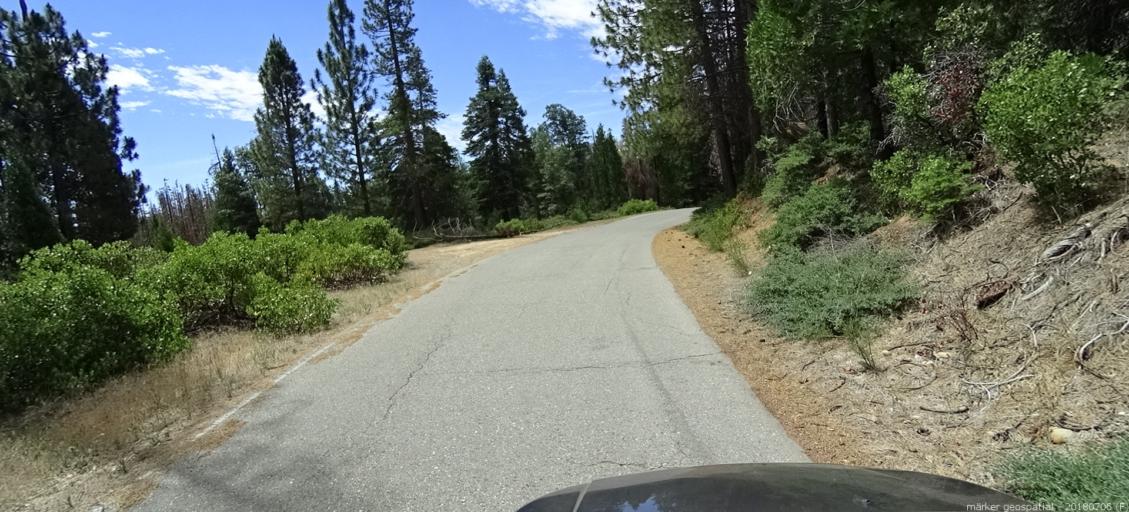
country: US
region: California
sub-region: Madera County
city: Oakhurst
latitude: 37.4230
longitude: -119.4125
